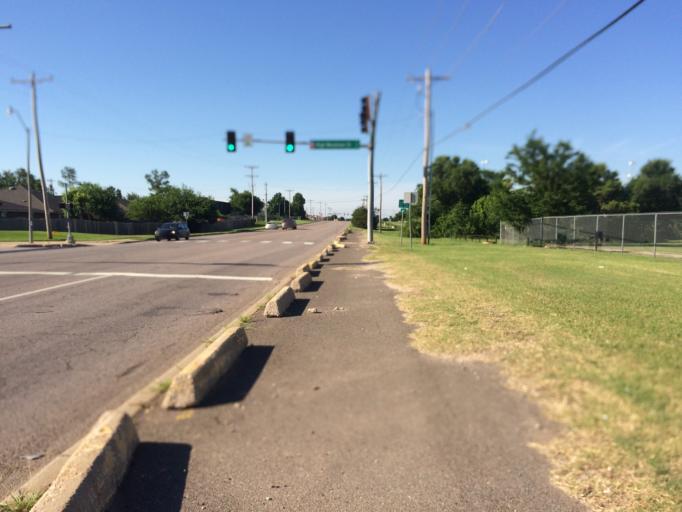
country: US
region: Oklahoma
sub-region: Cleveland County
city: Hall Park
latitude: 35.2374
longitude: -97.4237
